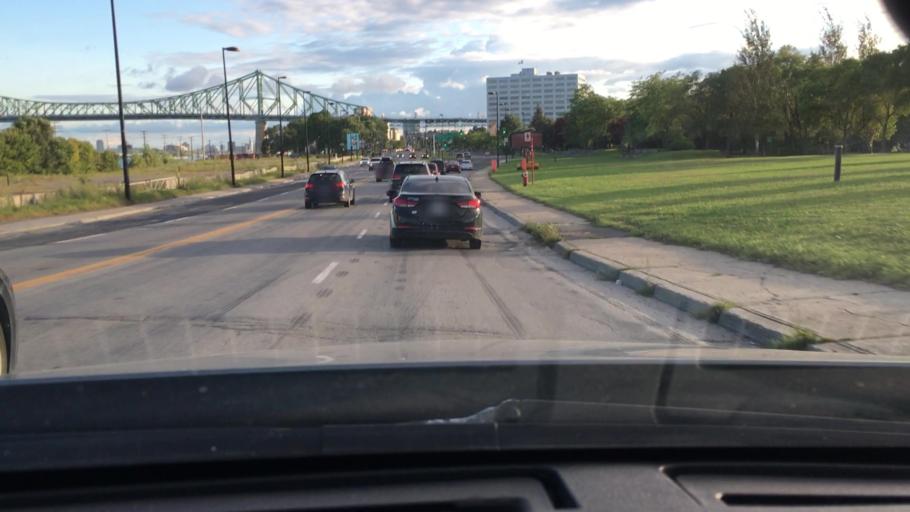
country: CA
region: Quebec
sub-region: Monteregie
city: Longueuil
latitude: 45.5312
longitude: -73.5434
